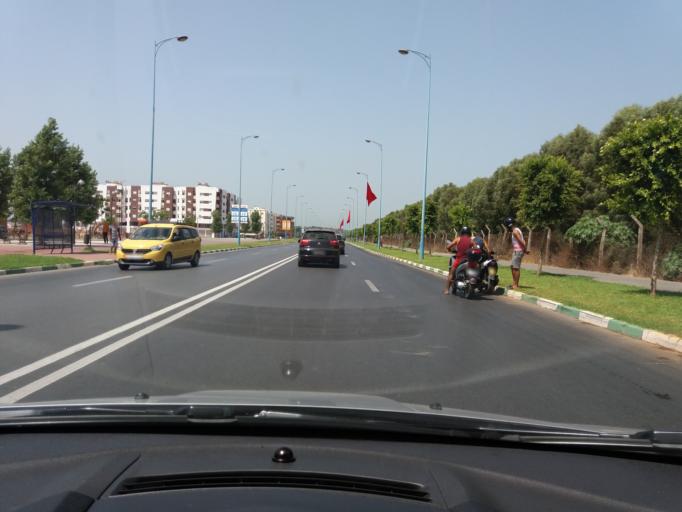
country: MA
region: Gharb-Chrarda-Beni Hssen
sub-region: Kenitra Province
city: Kenitra
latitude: 34.2726
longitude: -6.6248
